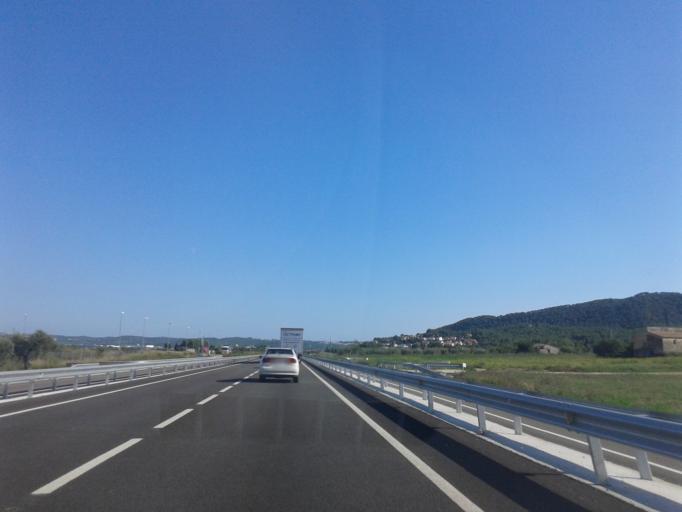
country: ES
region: Catalonia
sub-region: Provincia de Tarragona
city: Albinyana
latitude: 41.2539
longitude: 1.5069
